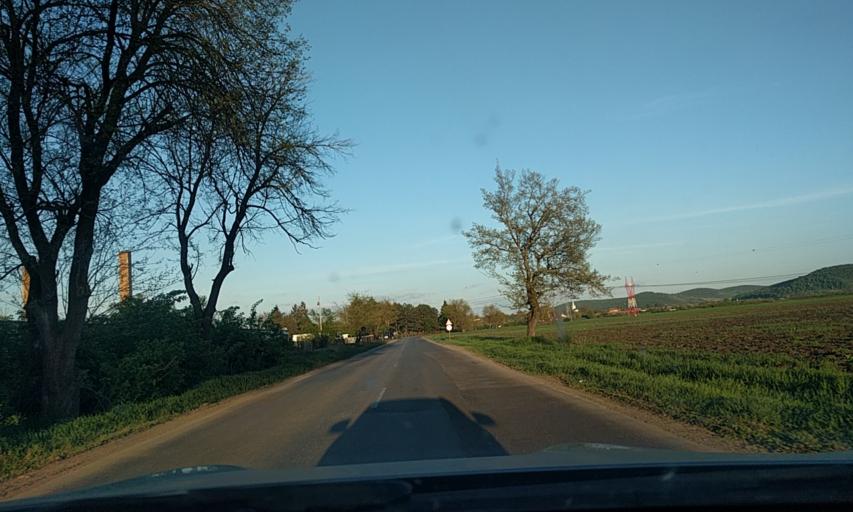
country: RO
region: Mures
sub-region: Comuna Ungheni
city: Ungheni
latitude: 46.4761
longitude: 24.4696
